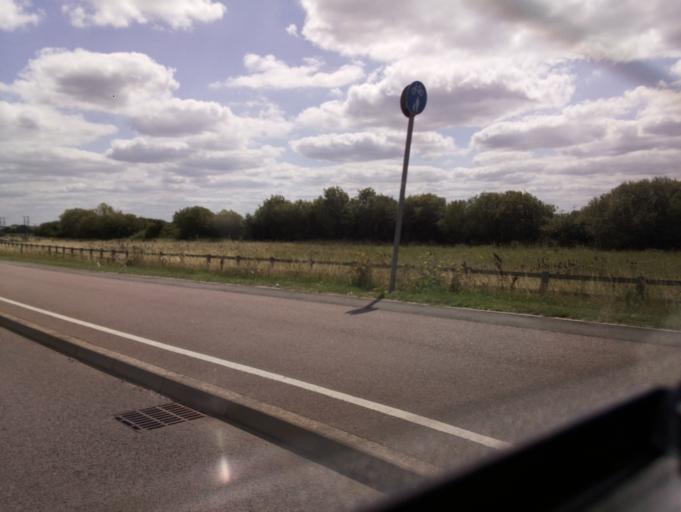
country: GB
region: England
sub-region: Buckinghamshire
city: Aylesbury
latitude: 51.8393
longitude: -0.8412
